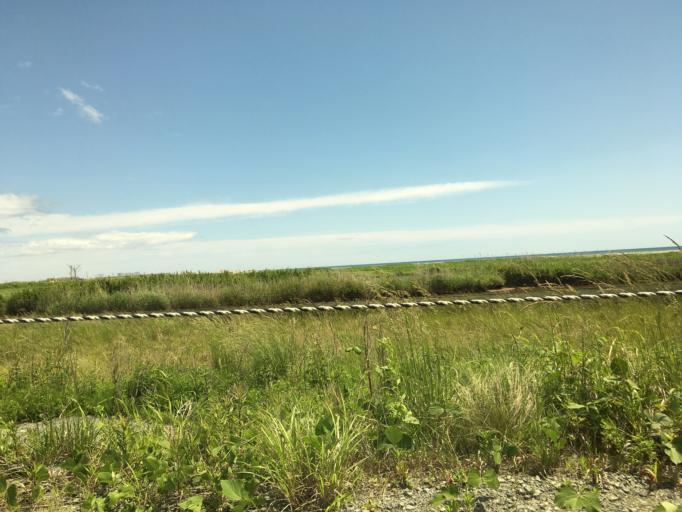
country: JP
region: Fukushima
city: Namie
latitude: 37.4584
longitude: 141.0327
